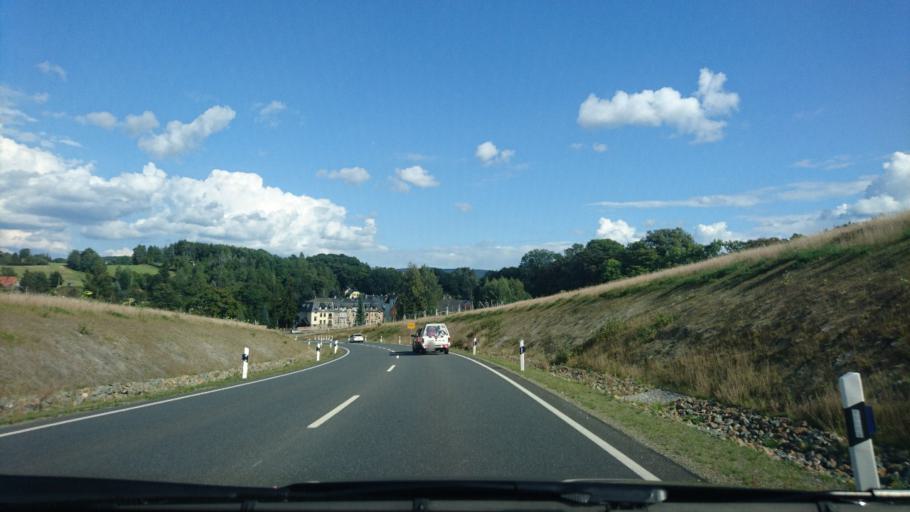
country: DE
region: Saxony
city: Rodewisch
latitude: 50.5354
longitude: 12.3983
